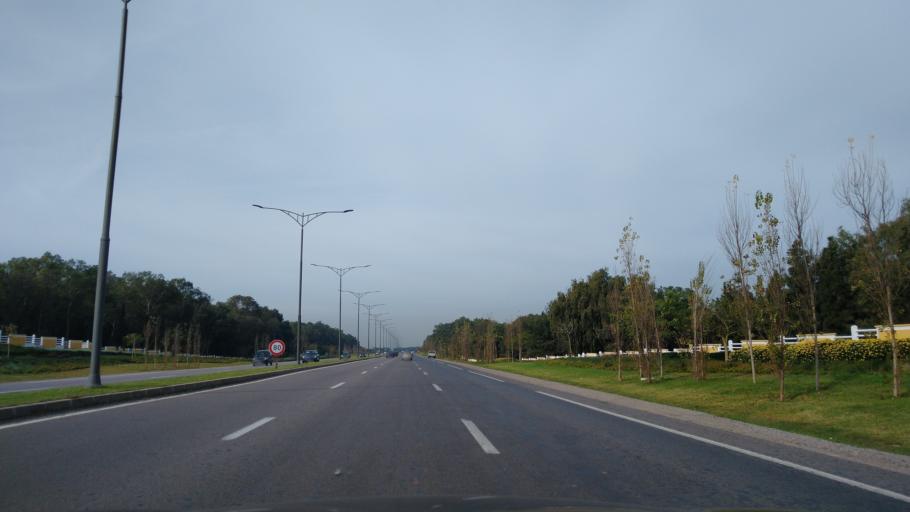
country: MA
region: Rabat-Sale-Zemmour-Zaer
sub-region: Skhirate-Temara
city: Temara
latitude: 33.9481
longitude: -6.9029
